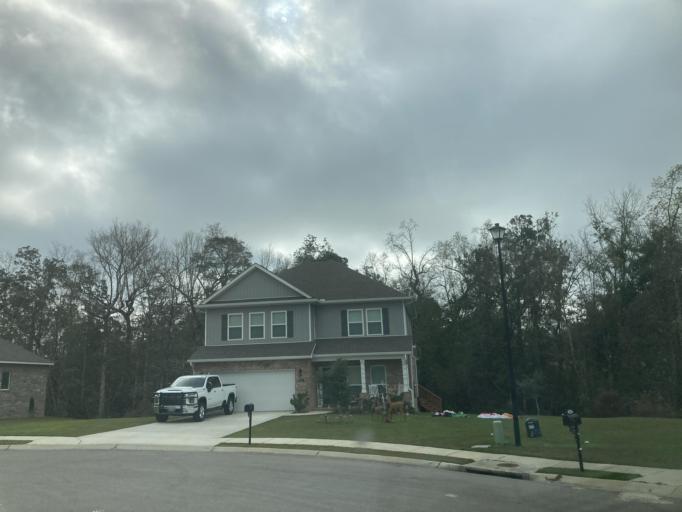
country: US
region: Mississippi
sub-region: Harrison County
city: D'Iberville
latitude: 30.4762
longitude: -88.9949
